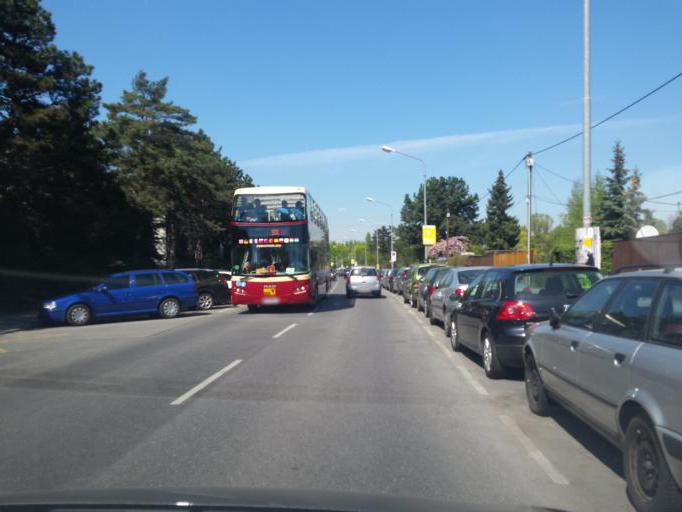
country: AT
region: Vienna
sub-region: Wien Stadt
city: Vienna
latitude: 48.2385
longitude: 16.4233
